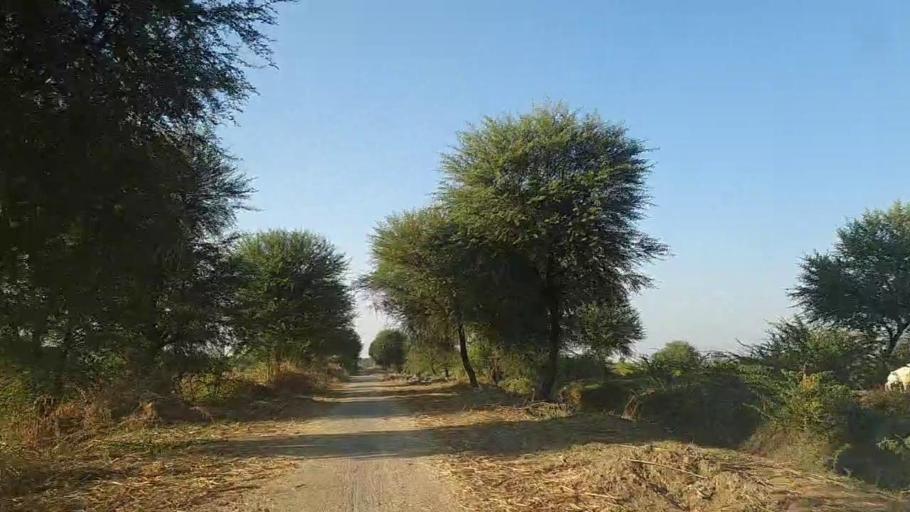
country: PK
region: Sindh
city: Samaro
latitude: 25.3443
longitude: 69.4135
